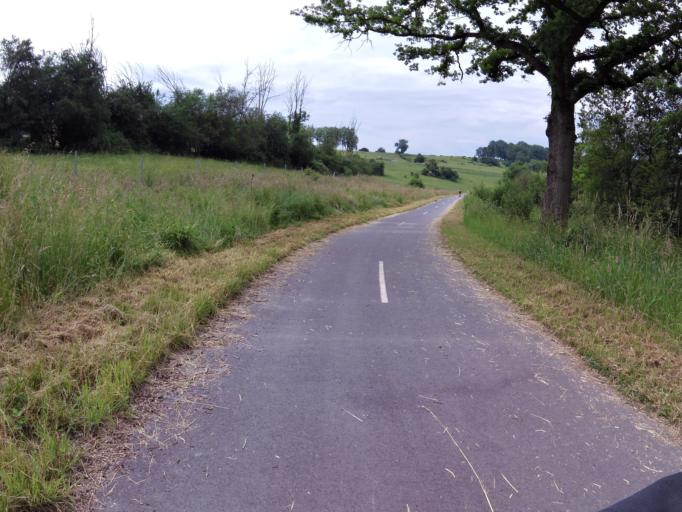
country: FR
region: Champagne-Ardenne
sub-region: Departement des Ardennes
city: Donchery
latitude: 49.6951
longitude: 4.8987
